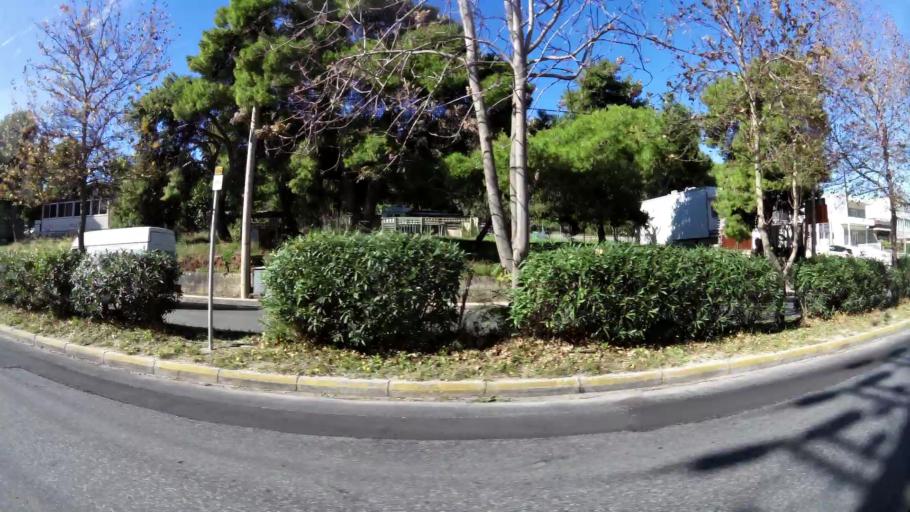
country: GR
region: Attica
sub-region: Nomarchia Anatolikis Attikis
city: Leondarion
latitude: 38.0030
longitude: 23.8479
